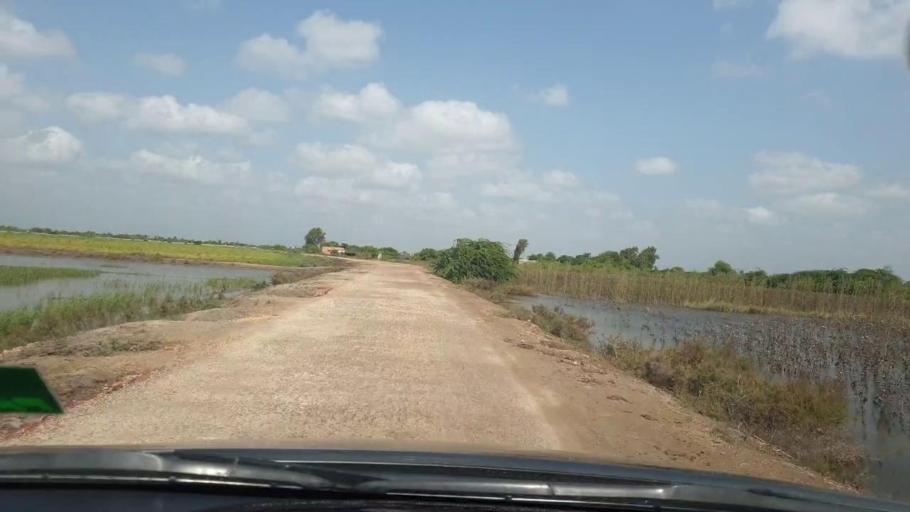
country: PK
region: Sindh
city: Tando Bago
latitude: 24.8641
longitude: 69.0574
